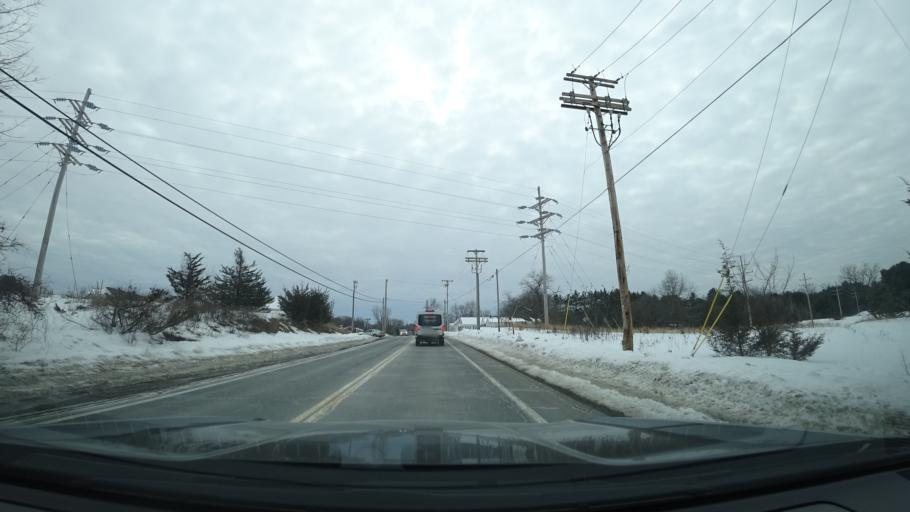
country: US
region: New York
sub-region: Saratoga County
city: South Glens Falls
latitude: 43.2872
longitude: -73.6242
